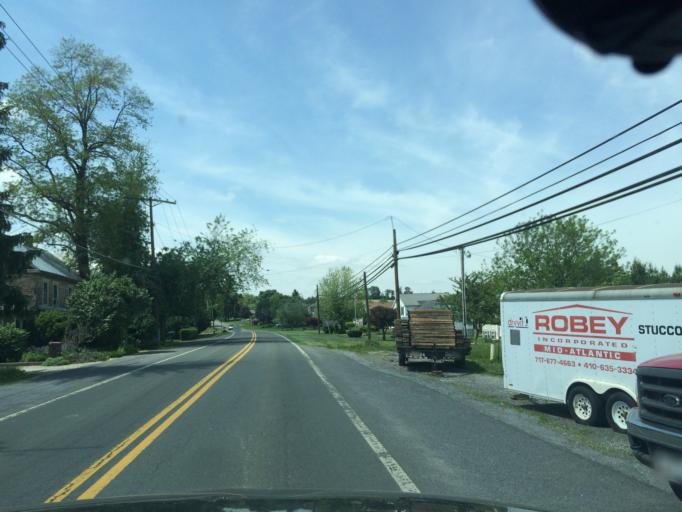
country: US
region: Maryland
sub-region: Carroll County
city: Westminster
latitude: 39.5434
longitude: -76.9377
